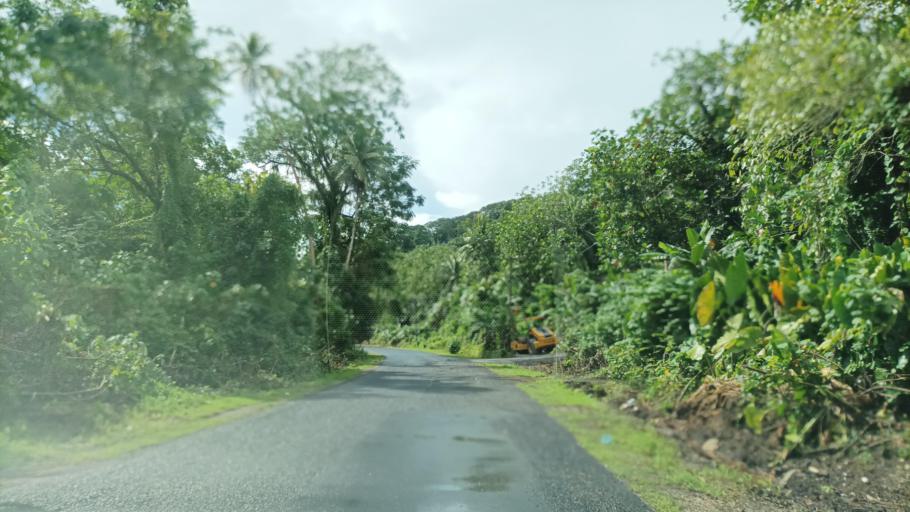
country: FM
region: Pohnpei
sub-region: Madolenihm Municipality
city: Madolenihm Municipality Government
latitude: 6.9152
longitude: 158.3210
